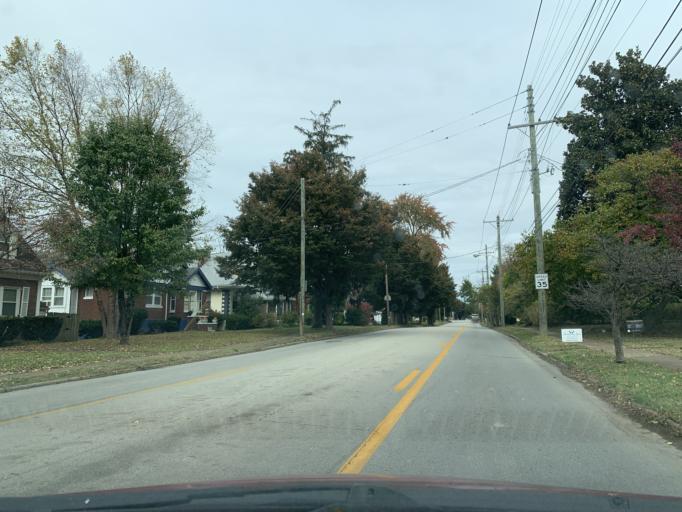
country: US
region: Kentucky
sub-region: Jefferson County
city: Audubon Park
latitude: 38.1789
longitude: -85.7667
